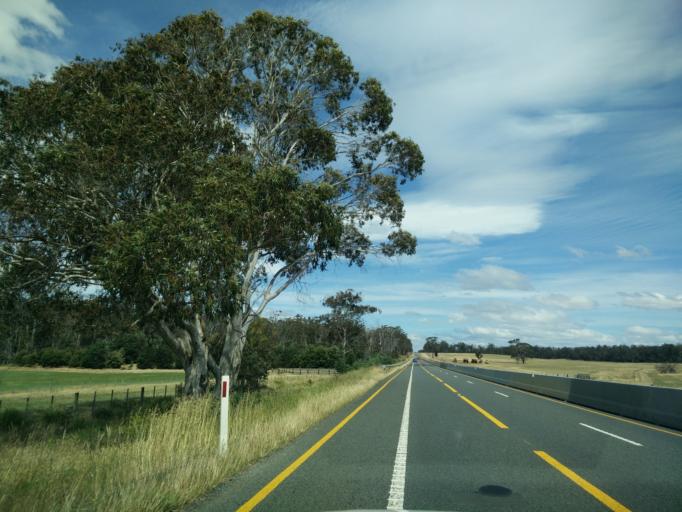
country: AU
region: Tasmania
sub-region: Northern Midlands
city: Evandale
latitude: -41.7409
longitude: 147.3322
